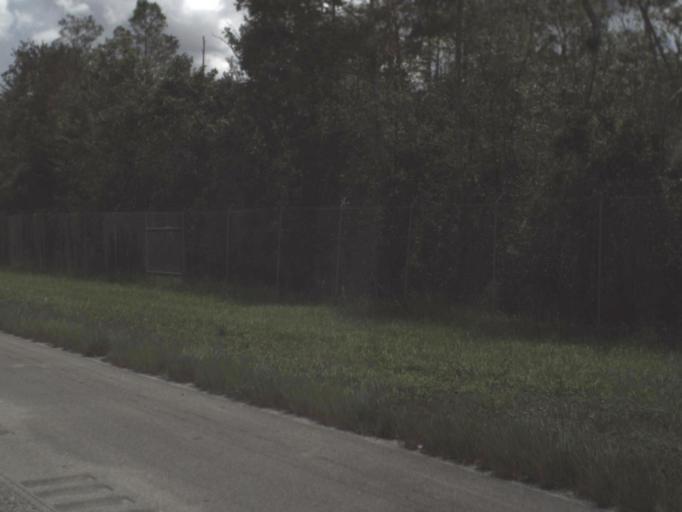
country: US
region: Florida
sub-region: Collier County
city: Immokalee
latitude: 26.1659
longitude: -81.2404
